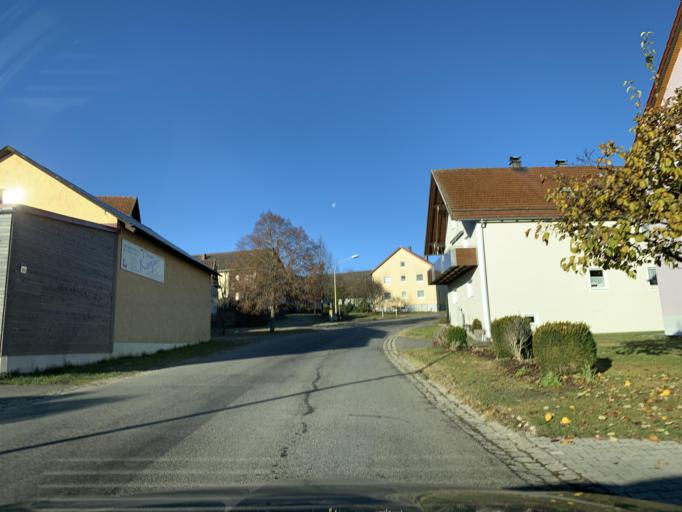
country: DE
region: Bavaria
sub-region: Upper Palatinate
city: Winklarn
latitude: 49.4642
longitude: 12.4676
